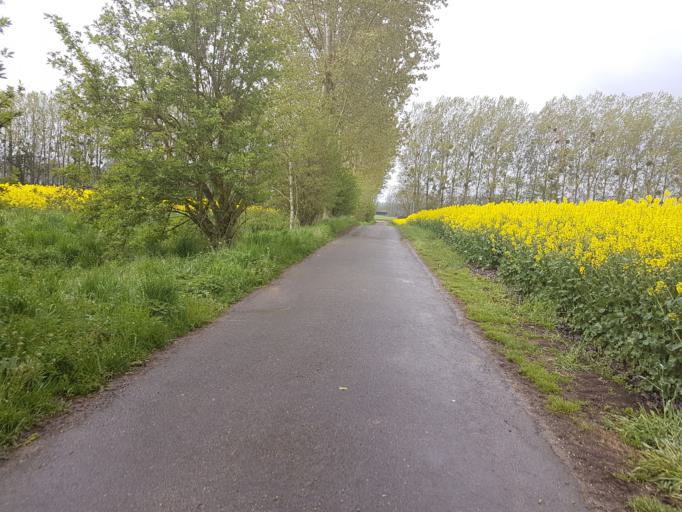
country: CH
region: Vaud
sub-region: Jura-Nord vaudois District
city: Montagny
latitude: 46.7578
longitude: 6.6124
